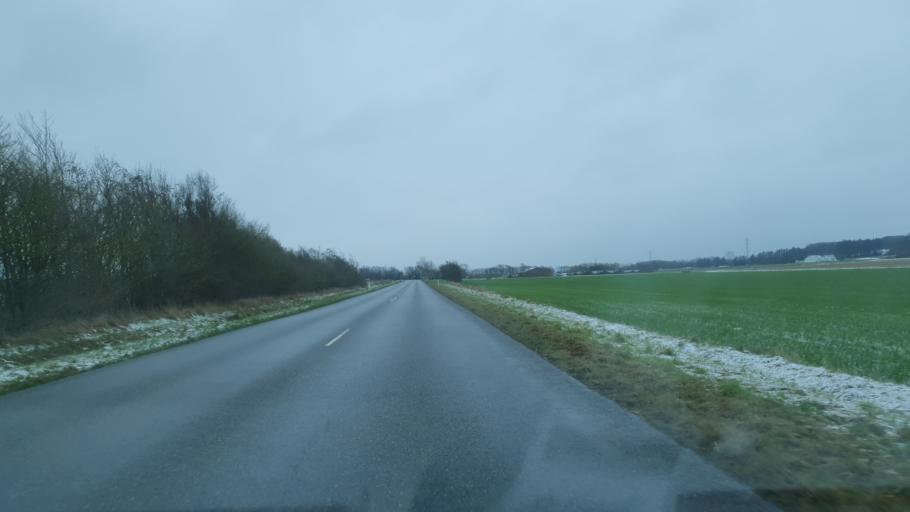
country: DK
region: North Denmark
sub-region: Jammerbugt Kommune
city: Brovst
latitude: 57.1061
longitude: 9.5020
